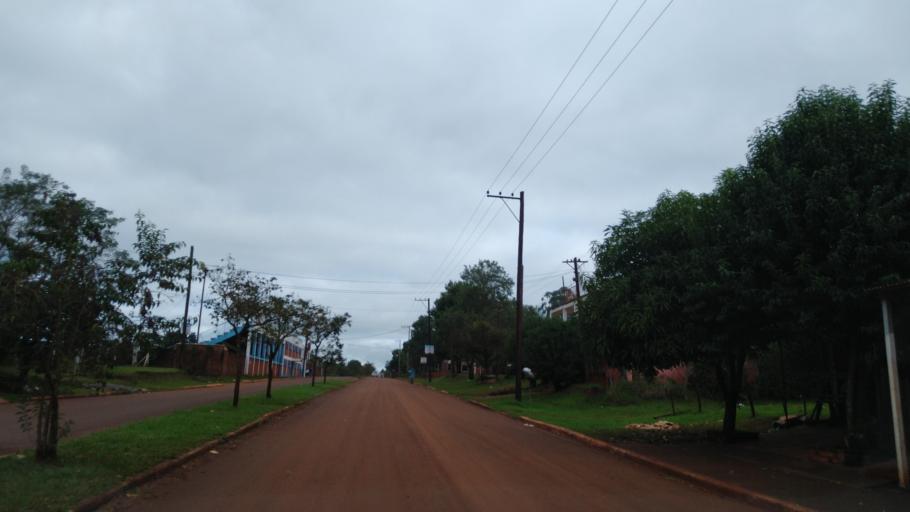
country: AR
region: Misiones
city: Jardin America
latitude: -27.0303
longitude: -55.2350
